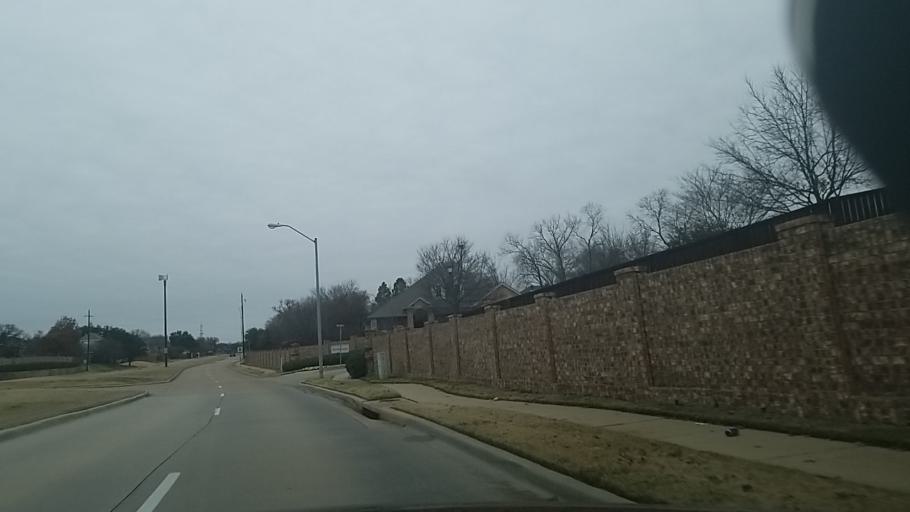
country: US
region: Texas
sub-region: Denton County
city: Corinth
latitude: 33.1346
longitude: -97.0736
